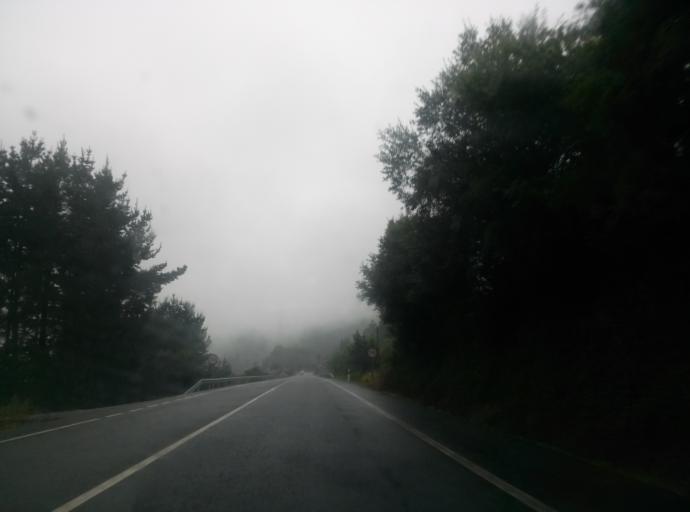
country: ES
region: Galicia
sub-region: Provincia de Lugo
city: Muras
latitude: 43.5462
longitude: -7.6523
